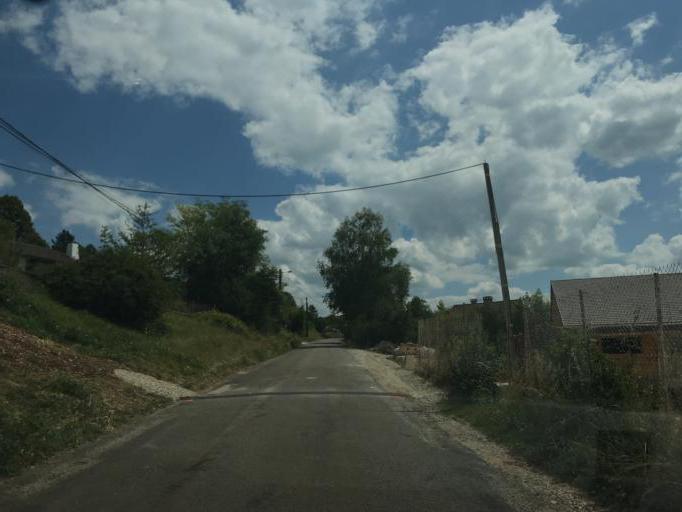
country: FR
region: Franche-Comte
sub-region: Departement du Jura
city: Clairvaux-les-Lacs
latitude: 46.5690
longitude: 5.7613
